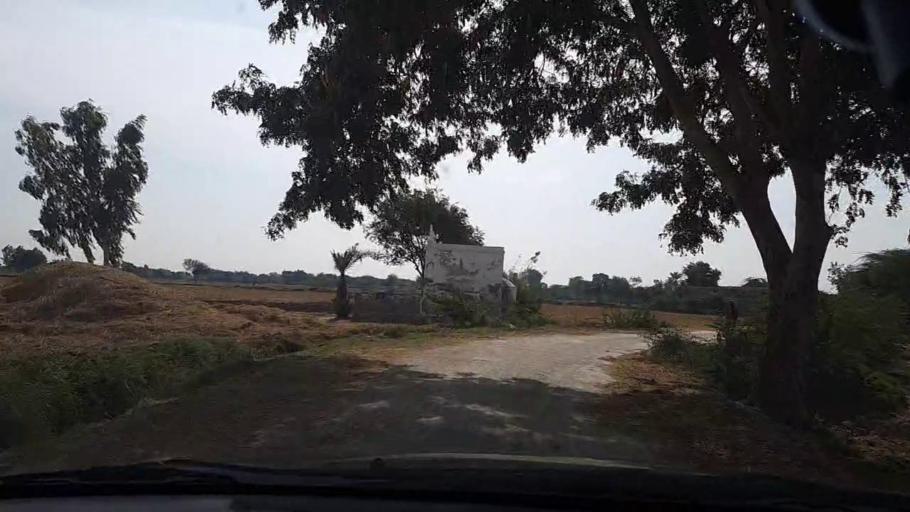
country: PK
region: Sindh
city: Mirpur Batoro
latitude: 24.7386
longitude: 68.2707
